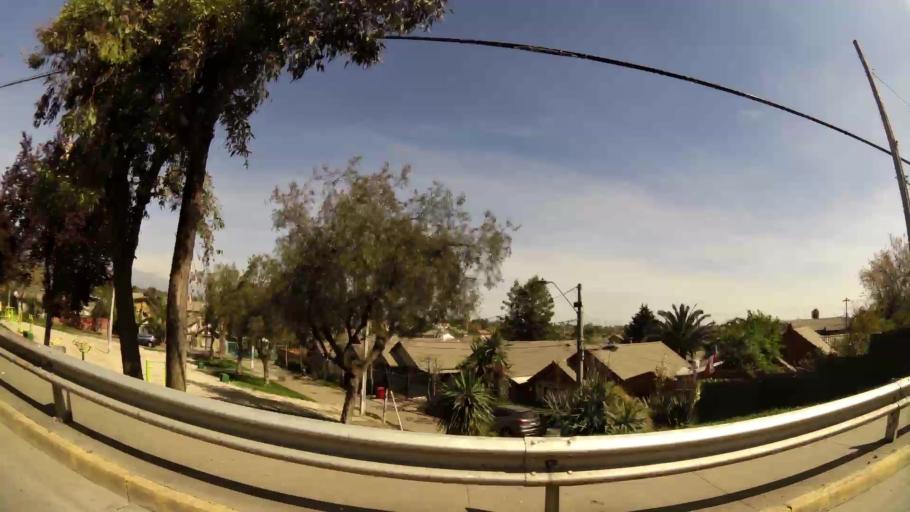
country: CL
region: Santiago Metropolitan
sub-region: Provincia de Cordillera
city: Puente Alto
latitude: -33.5357
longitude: -70.5595
